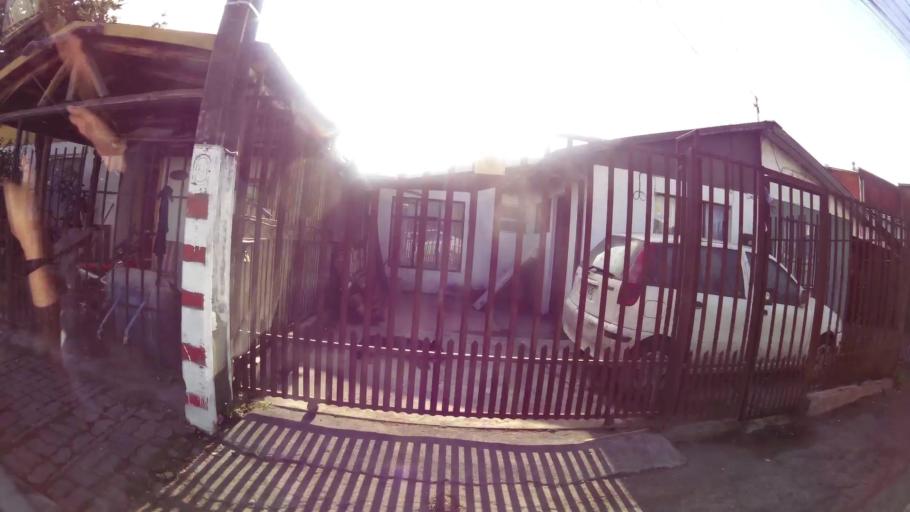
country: CL
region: Biobio
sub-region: Provincia de Concepcion
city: Concepcion
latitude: -36.7890
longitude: -73.0960
